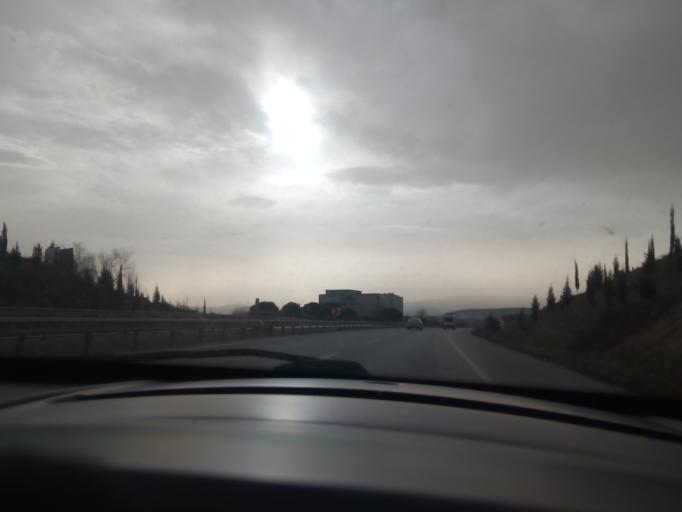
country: TR
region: Bursa
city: Tatkavakli
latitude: 40.0457
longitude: 28.3765
